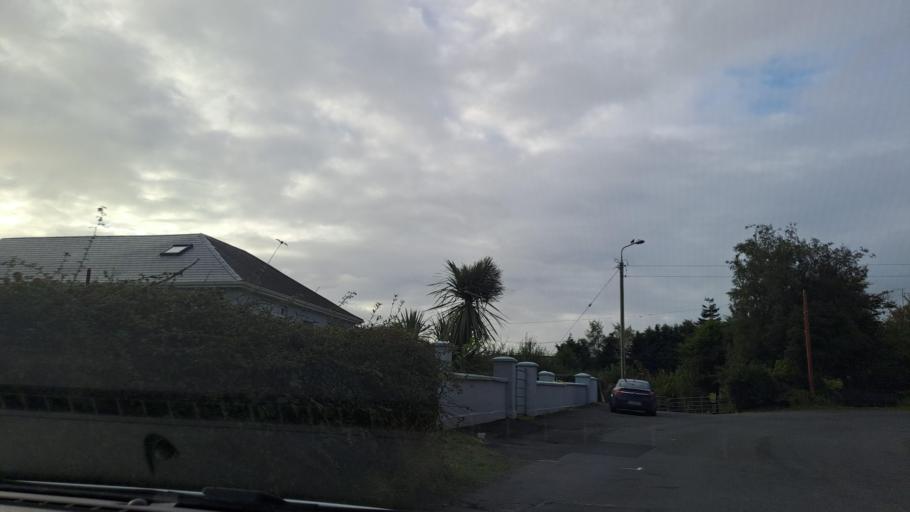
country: IE
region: Ulster
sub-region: An Cabhan
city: Bailieborough
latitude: 53.9950
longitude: -6.8937
